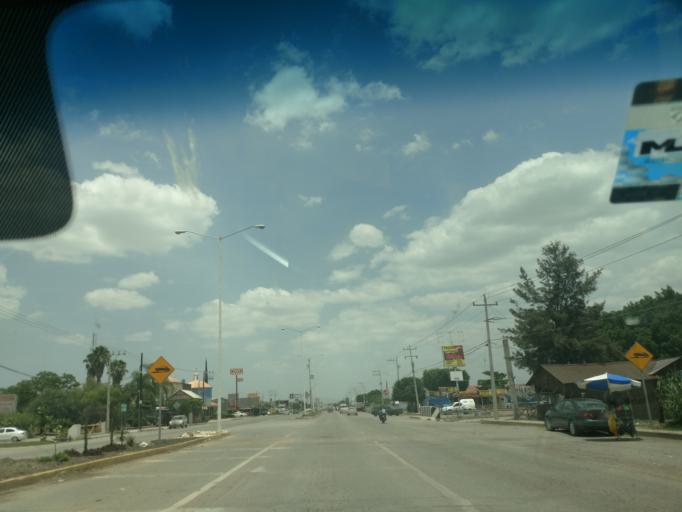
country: MX
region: San Luis Potosi
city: Ciudad Fernandez
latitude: 21.9371
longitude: -100.0303
